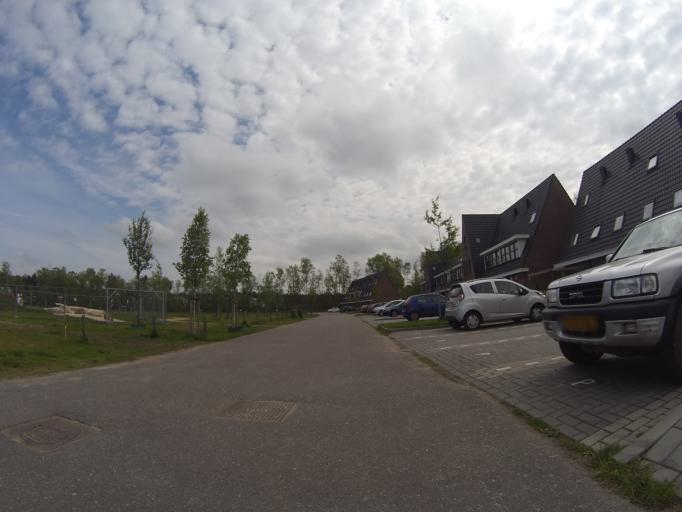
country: NL
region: Utrecht
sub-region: Gemeente Utrechtse Heuvelrug
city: Maarsbergen
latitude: 52.0552
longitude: 5.4101
